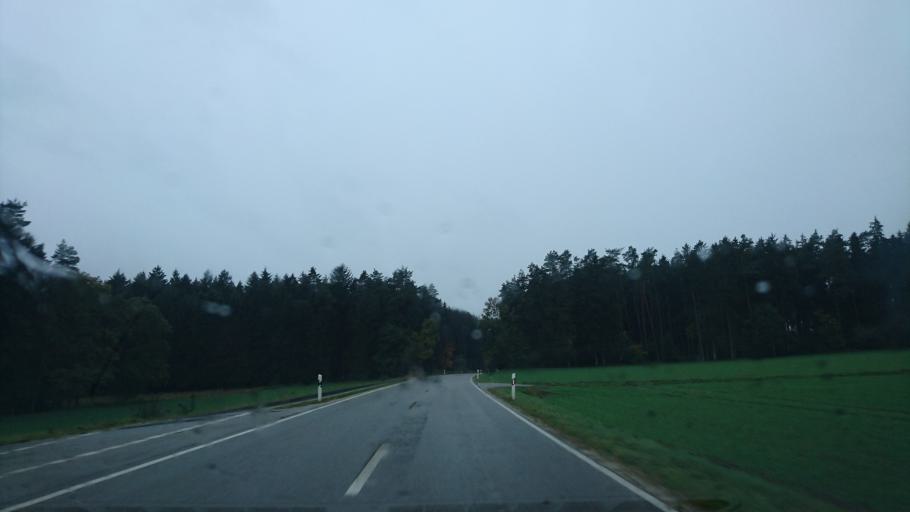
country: DE
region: Bavaria
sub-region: Swabia
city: Kuhbach
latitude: 48.4562
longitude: 11.1935
